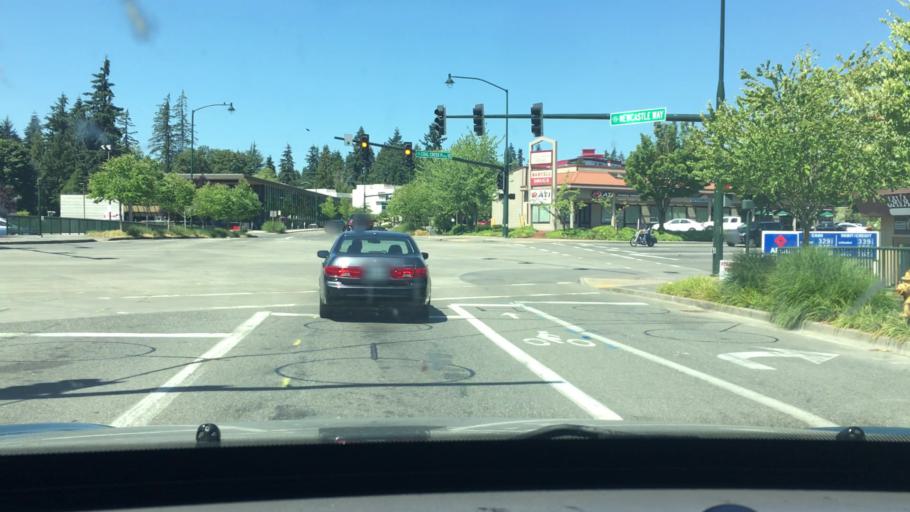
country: US
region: Washington
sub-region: King County
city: Newcastle
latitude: 47.5377
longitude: -122.1653
